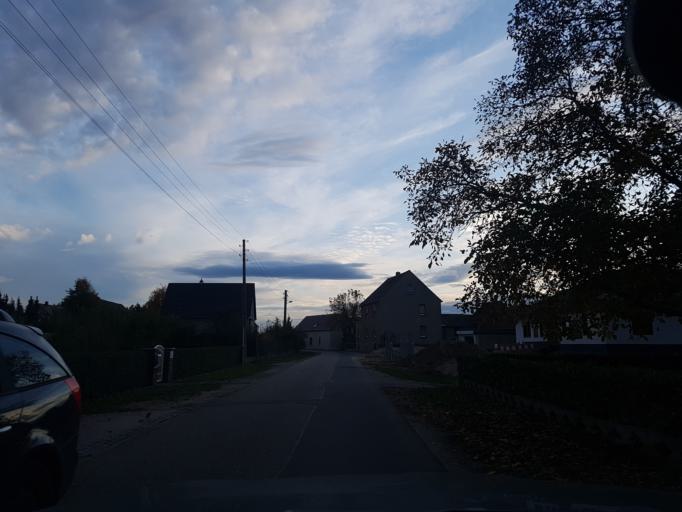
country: DE
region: Brandenburg
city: Elsterwerda
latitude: 51.4616
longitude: 13.4652
